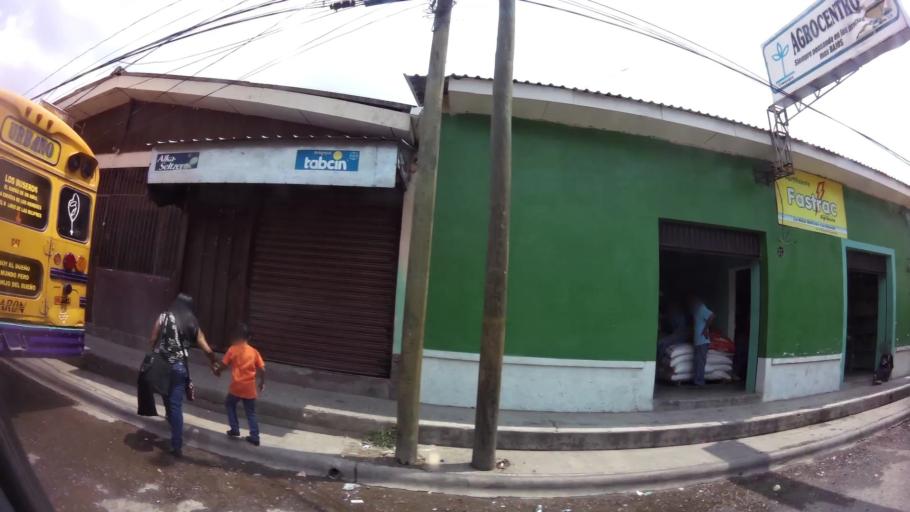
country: HN
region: Comayagua
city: Siguatepeque
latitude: 14.5991
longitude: -87.8318
